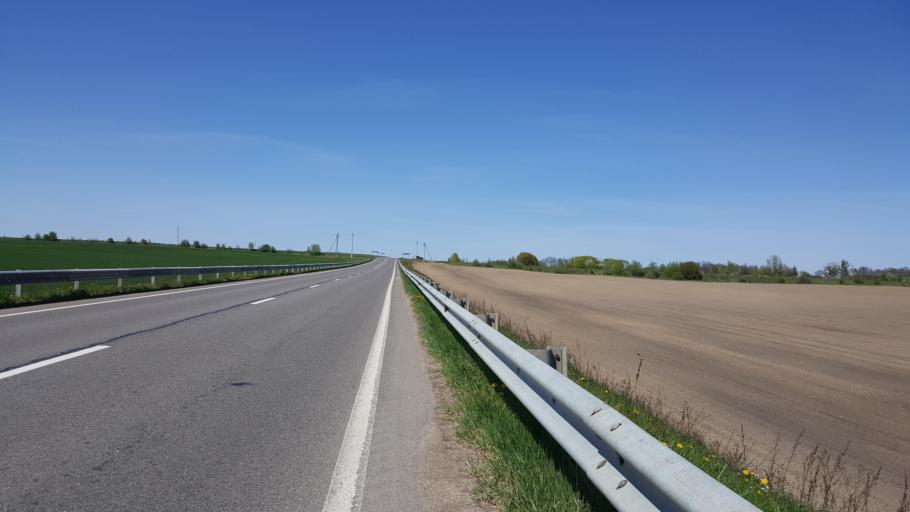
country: BY
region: Brest
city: Kamyanyets
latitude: 52.4306
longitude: 23.8351
